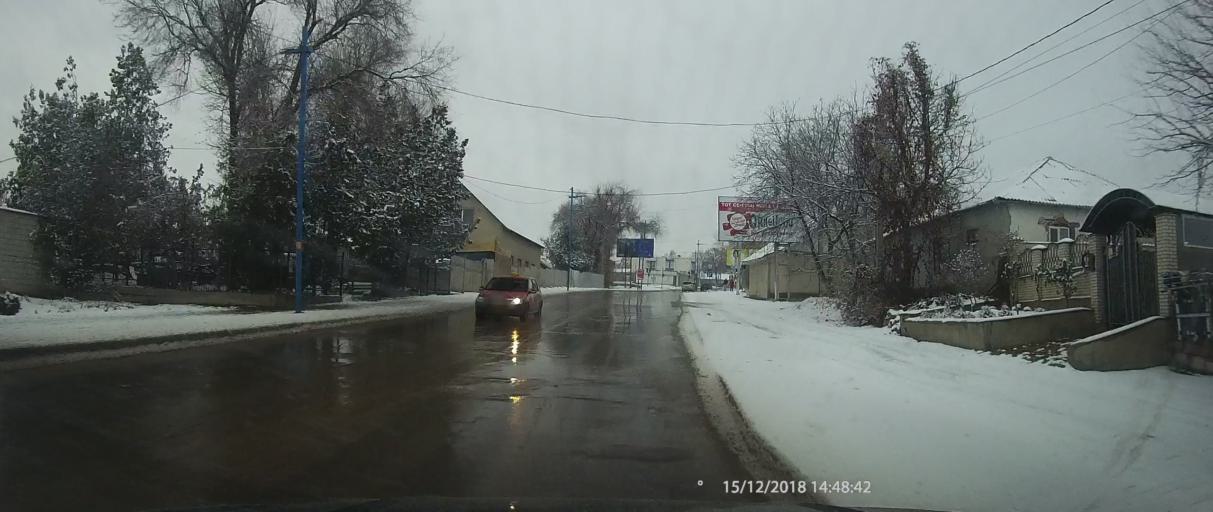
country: MD
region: Cahul
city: Cahul
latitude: 45.8993
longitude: 28.1967
